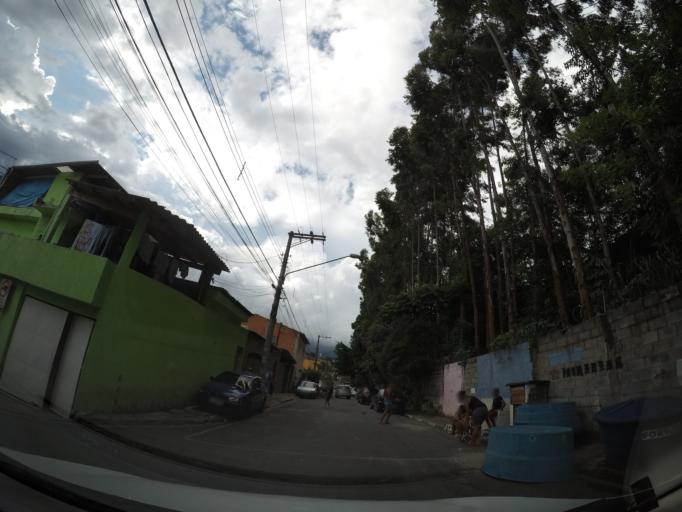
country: BR
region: Sao Paulo
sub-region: Guarulhos
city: Guarulhos
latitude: -23.4754
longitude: -46.5584
